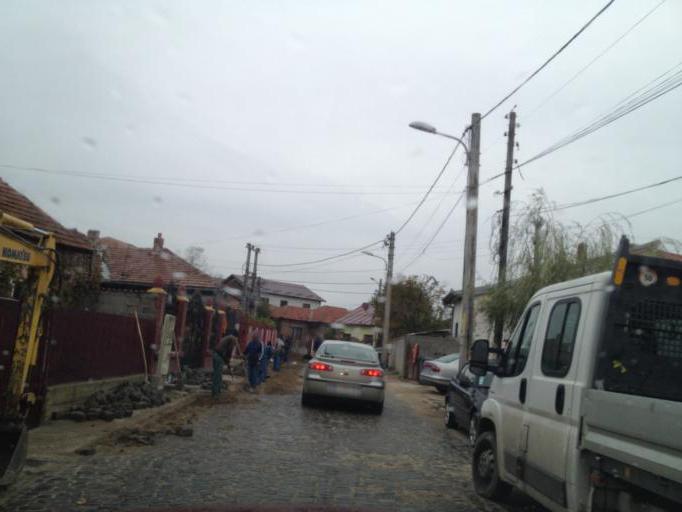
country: RO
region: Dolj
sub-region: Municipiul Craiova
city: Mofleni
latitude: 44.3140
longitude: 23.7680
